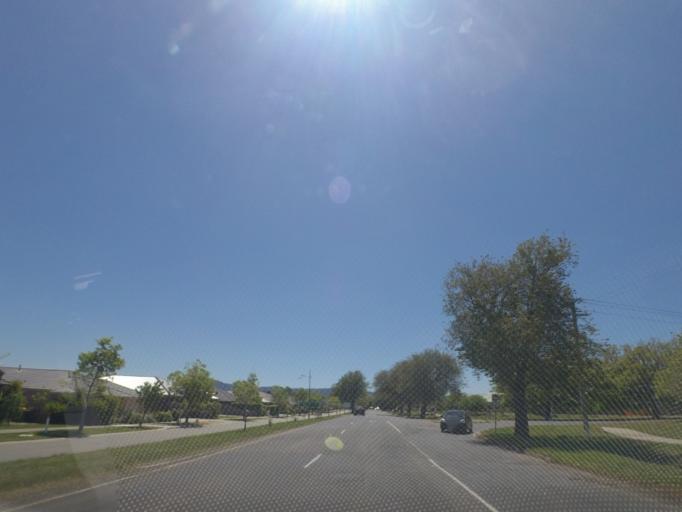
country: AU
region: Victoria
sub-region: Hume
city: Sunbury
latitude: -37.4696
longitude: 144.5944
